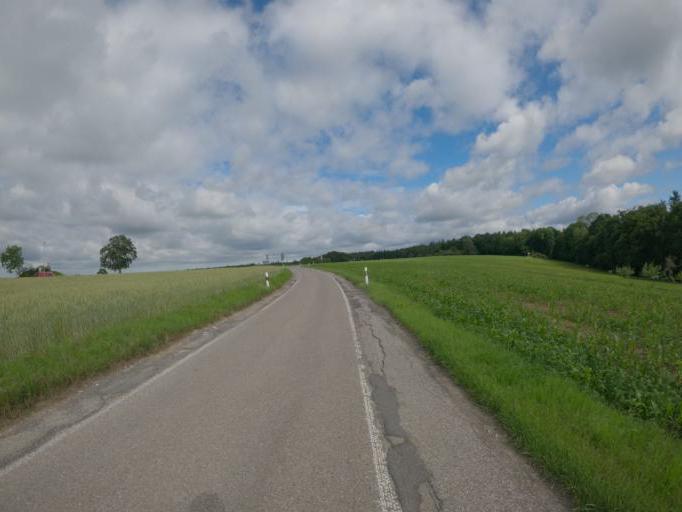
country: DE
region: Baden-Wuerttemberg
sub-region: Regierungsbezirk Stuttgart
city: Ebersbach an der Fils
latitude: 48.7347
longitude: 9.5332
